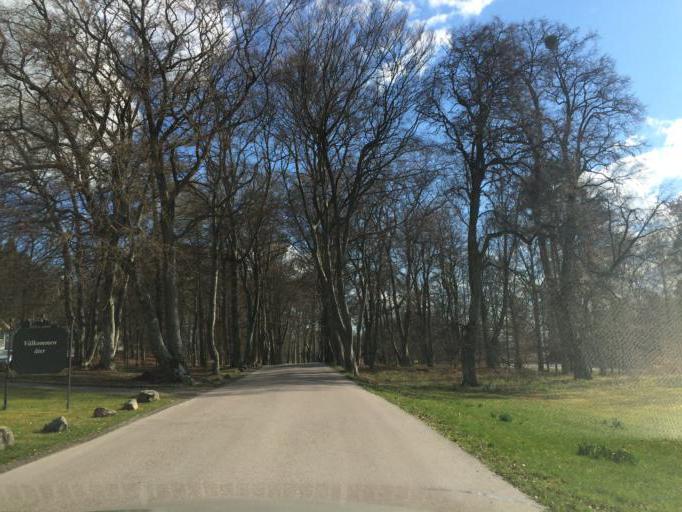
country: SE
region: Soedermanland
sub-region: Eskilstuna Kommun
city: Eskilstuna
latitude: 59.4459
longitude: 16.6231
